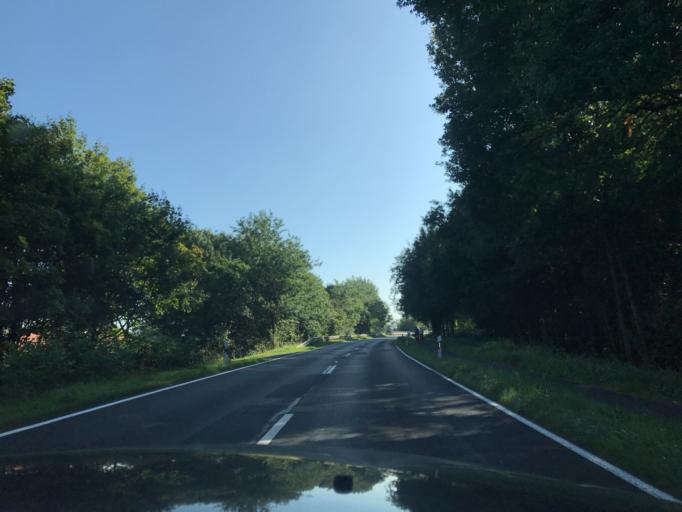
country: DE
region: Lower Saxony
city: Haselunne
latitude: 52.6584
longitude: 7.4339
